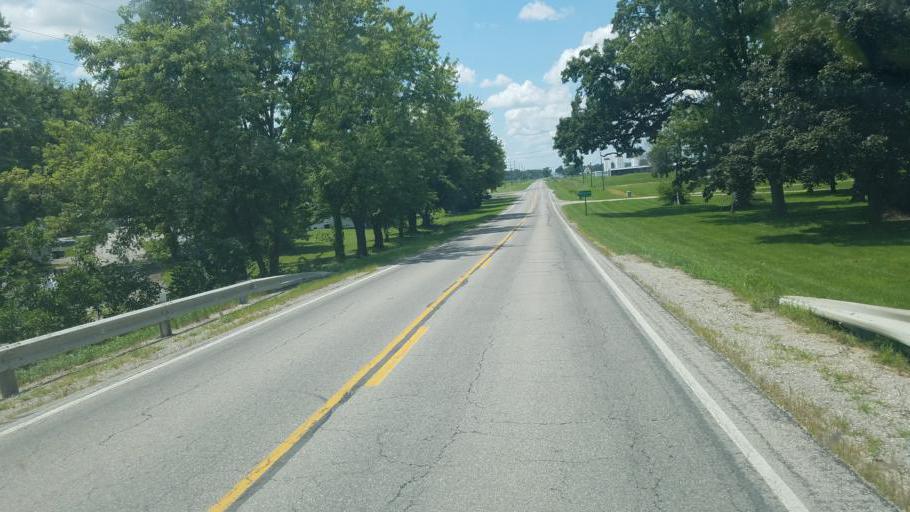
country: US
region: Ohio
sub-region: Marion County
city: Marion
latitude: 40.6298
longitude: -83.0987
